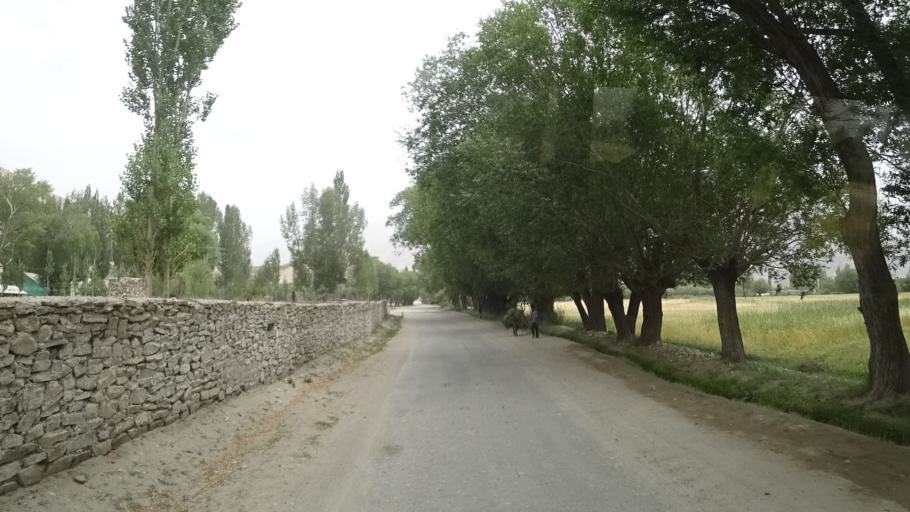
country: AF
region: Badakhshan
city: Khandud
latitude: 37.0384
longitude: 72.6526
